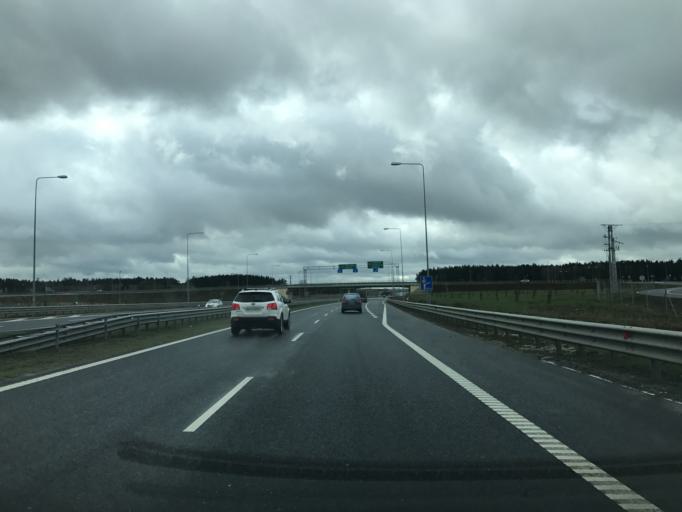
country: PL
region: Warmian-Masurian Voivodeship
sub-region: Powiat olsztynski
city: Olsztynek
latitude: 53.6048
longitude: 20.3093
